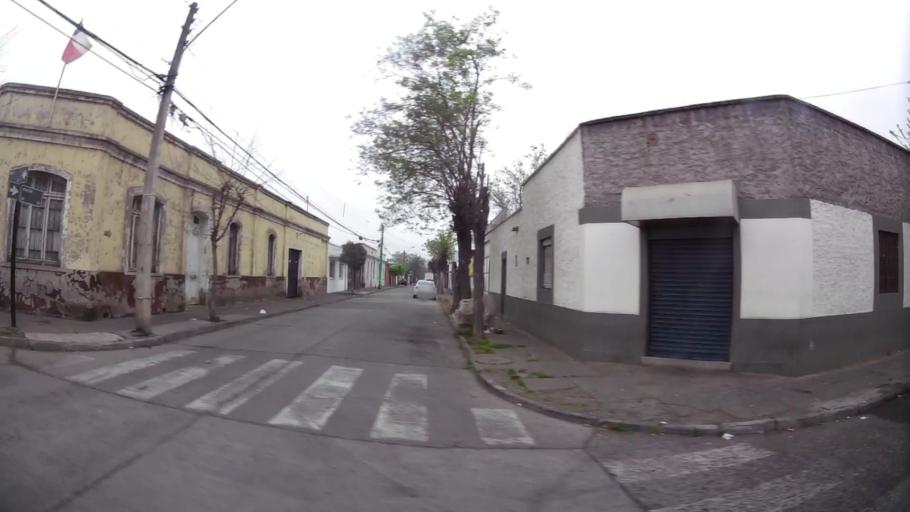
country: CL
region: Santiago Metropolitan
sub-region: Provincia de Santiago
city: Santiago
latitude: -33.4963
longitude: -70.6417
